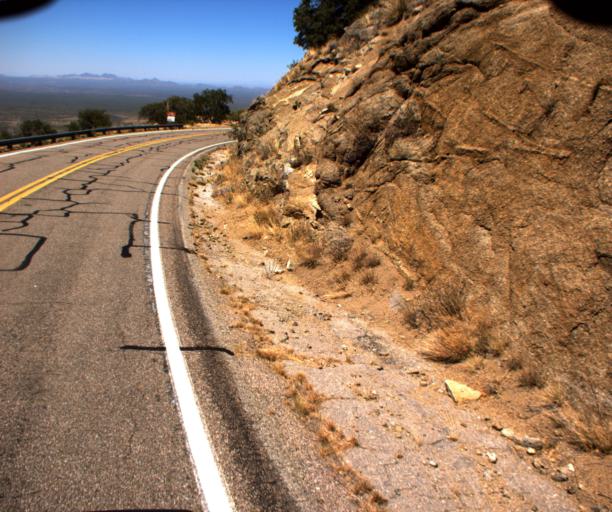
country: US
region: Arizona
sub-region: Pima County
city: Sells
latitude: 31.9743
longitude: -111.6093
